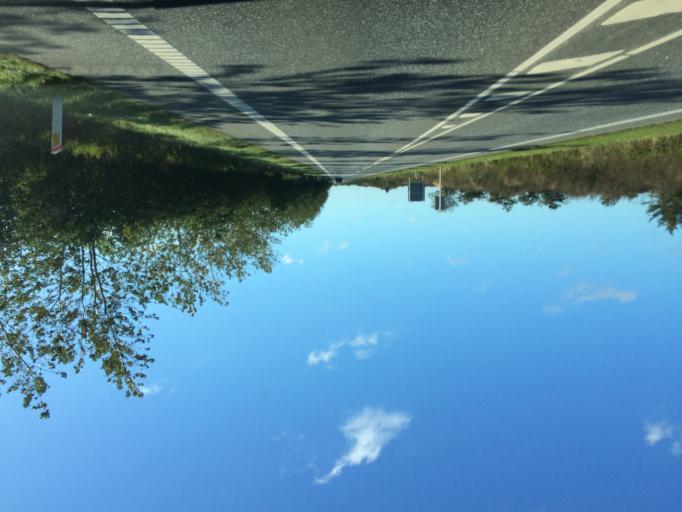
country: DK
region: Central Jutland
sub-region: Holstebro Kommune
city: Vinderup
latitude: 56.3993
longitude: 8.9092
